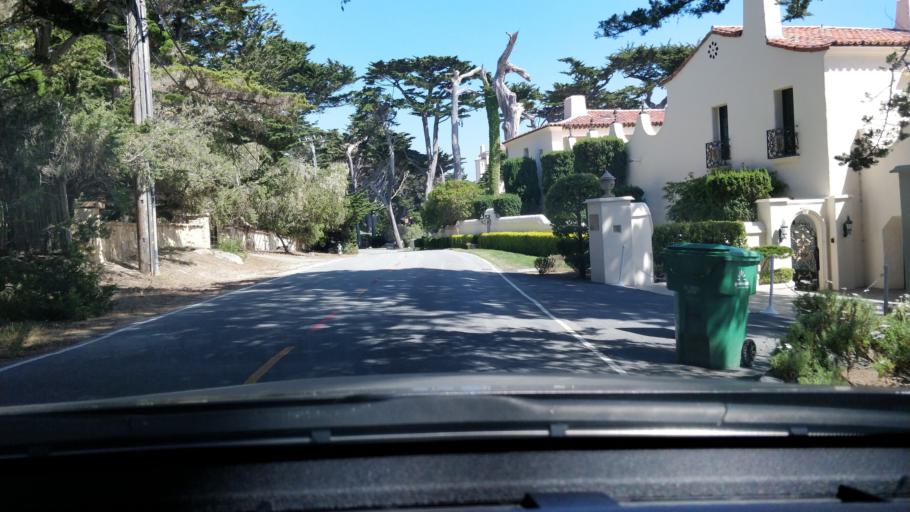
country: US
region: California
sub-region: Monterey County
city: Del Monte Forest
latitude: 36.5665
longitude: -121.9592
